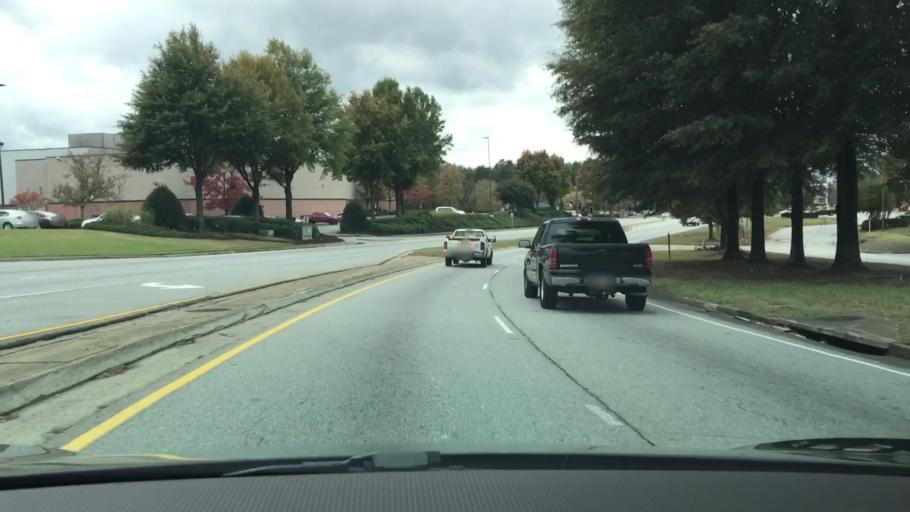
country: US
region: Georgia
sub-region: Gwinnett County
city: Lawrenceville
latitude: 33.9704
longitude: -84.0188
